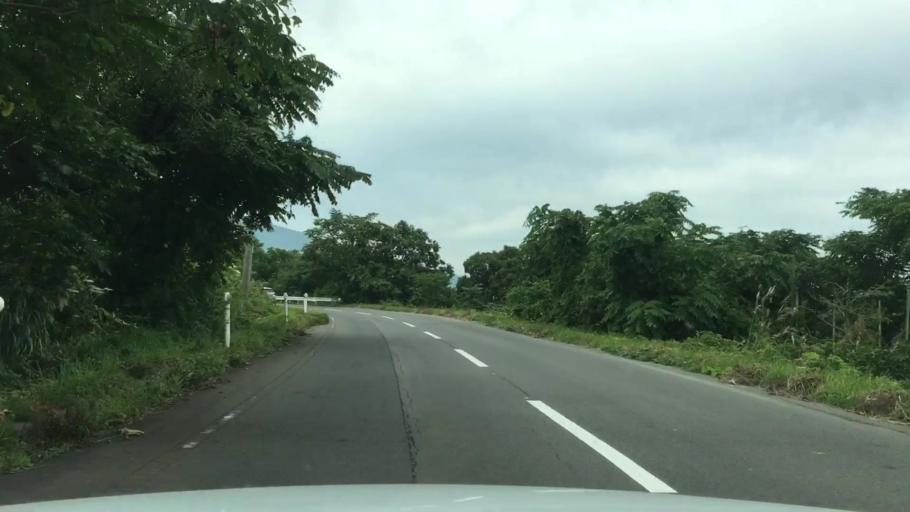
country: JP
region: Aomori
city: Hirosaki
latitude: 40.6672
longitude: 140.3984
